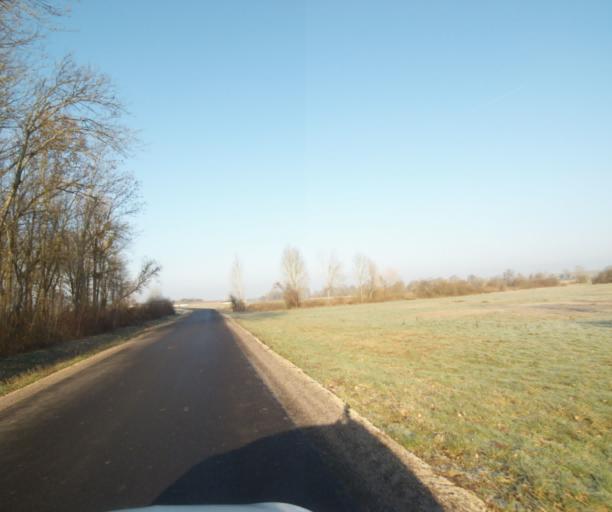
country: FR
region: Champagne-Ardenne
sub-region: Departement de la Haute-Marne
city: Montier-en-Der
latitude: 48.4916
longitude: 4.7336
